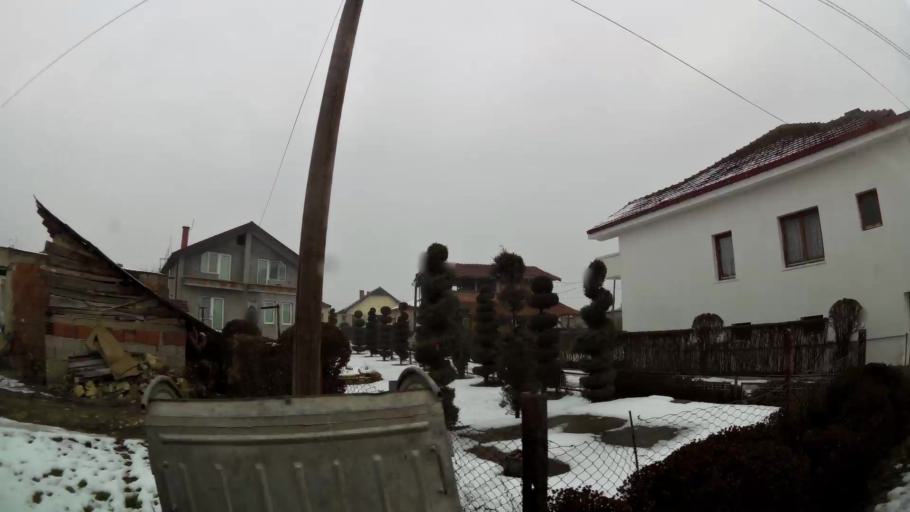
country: MK
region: Petrovec
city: Petrovec
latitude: 41.9415
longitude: 21.6131
